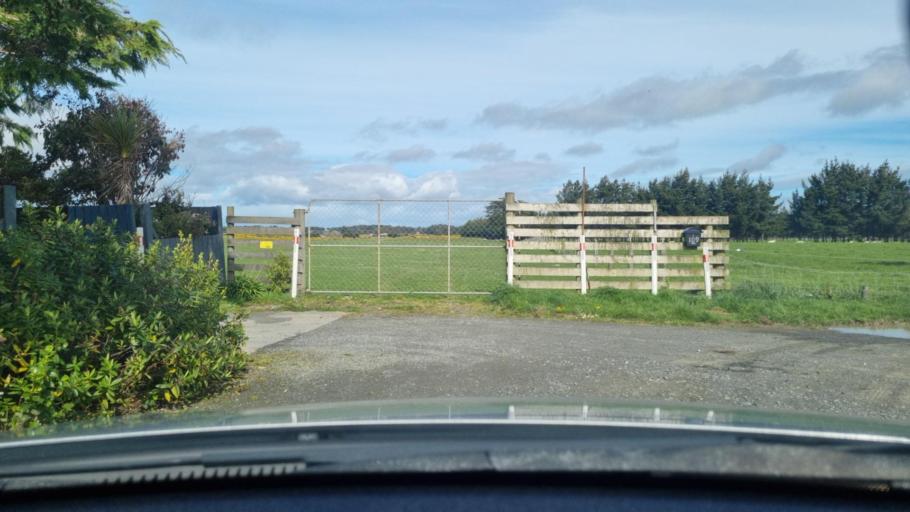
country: NZ
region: Southland
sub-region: Invercargill City
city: Invercargill
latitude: -46.4549
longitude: 168.3713
